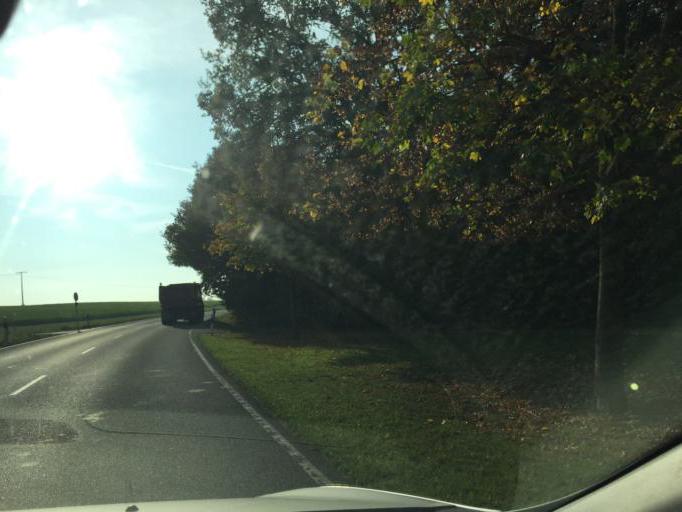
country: LU
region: Luxembourg
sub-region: Canton de Luxembourg
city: Contern
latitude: 49.5572
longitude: 6.2259
